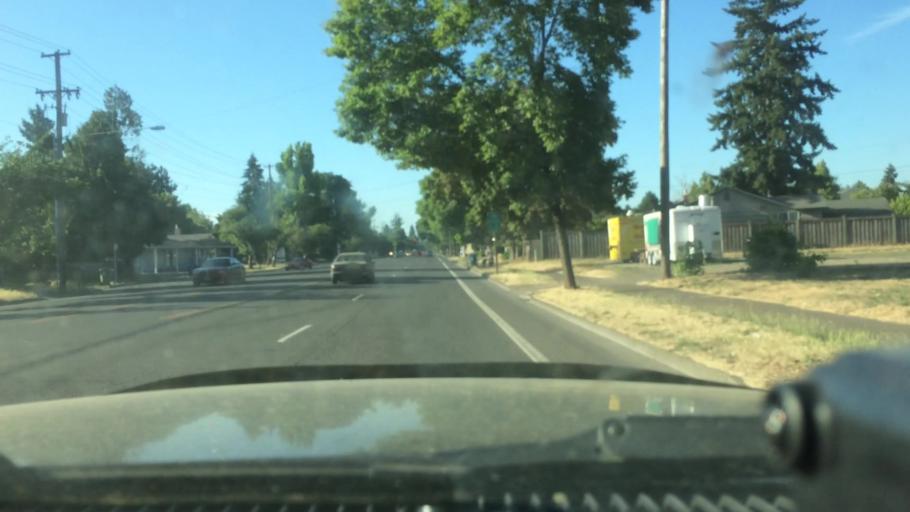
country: US
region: Oregon
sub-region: Lane County
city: Eugene
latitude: 44.0934
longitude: -123.1273
